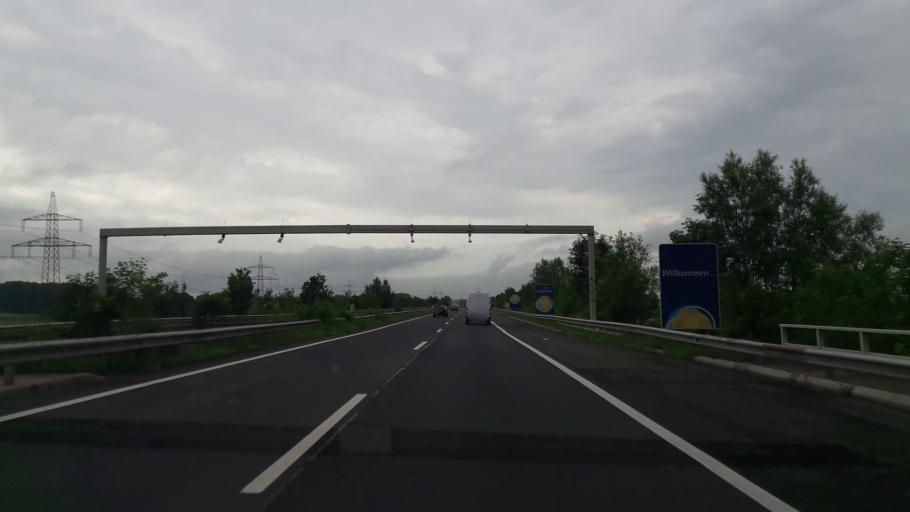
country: AT
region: Burgenland
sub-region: Eisenstadt-Umgebung
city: Wimpassing an der Leitha
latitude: 47.8953
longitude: 16.4143
